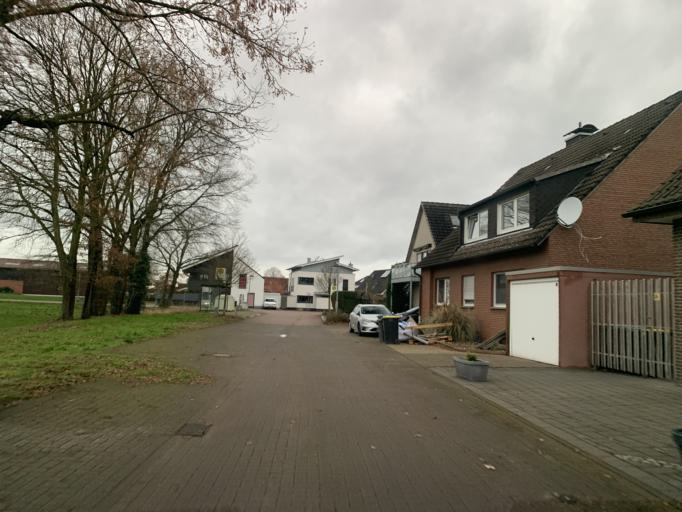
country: DE
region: North Rhine-Westphalia
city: Olfen
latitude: 51.7330
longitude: 7.2922
